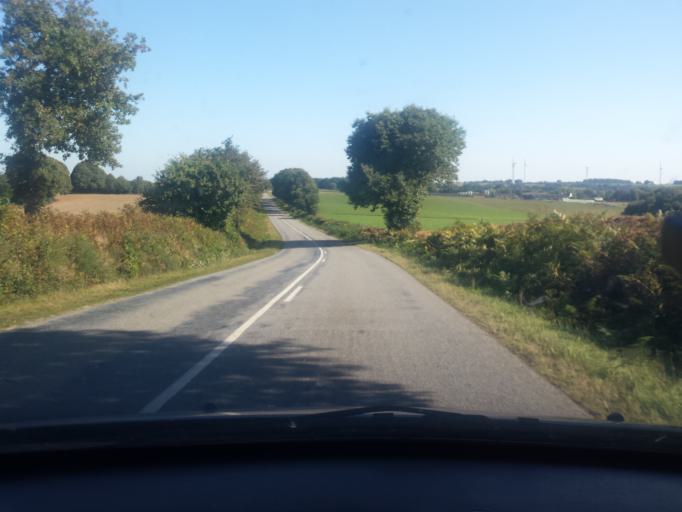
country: FR
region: Brittany
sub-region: Departement du Morbihan
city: Cleguerec
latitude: 48.1201
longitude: -3.1328
